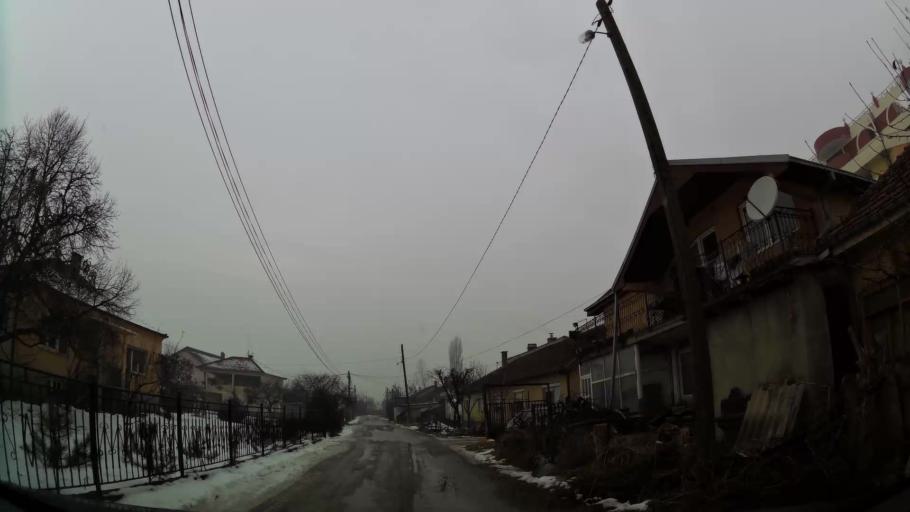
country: MK
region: Petrovec
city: Petrovec
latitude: 41.9380
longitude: 21.6153
